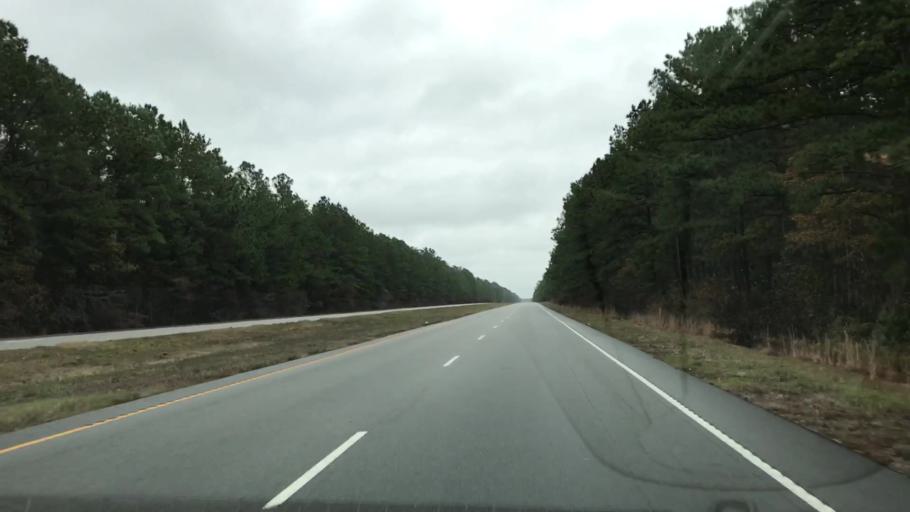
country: US
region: South Carolina
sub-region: Charleston County
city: Awendaw
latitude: 33.1499
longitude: -79.4334
